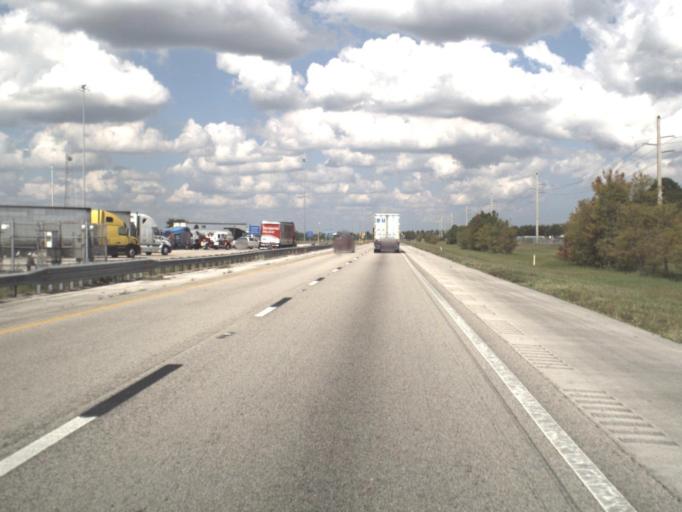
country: US
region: Florida
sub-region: Saint Lucie County
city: Port Saint Lucie
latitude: 27.3015
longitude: -80.3717
